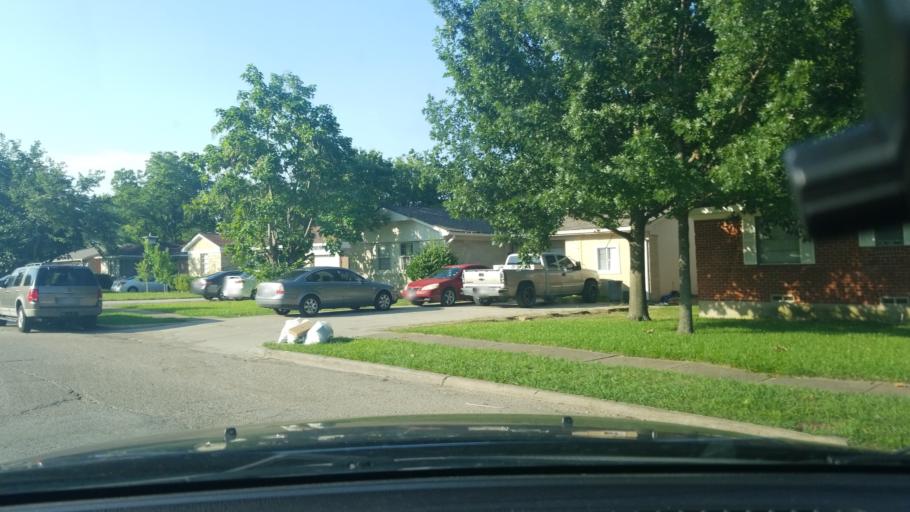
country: US
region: Texas
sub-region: Dallas County
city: Mesquite
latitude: 32.8112
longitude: -96.6417
